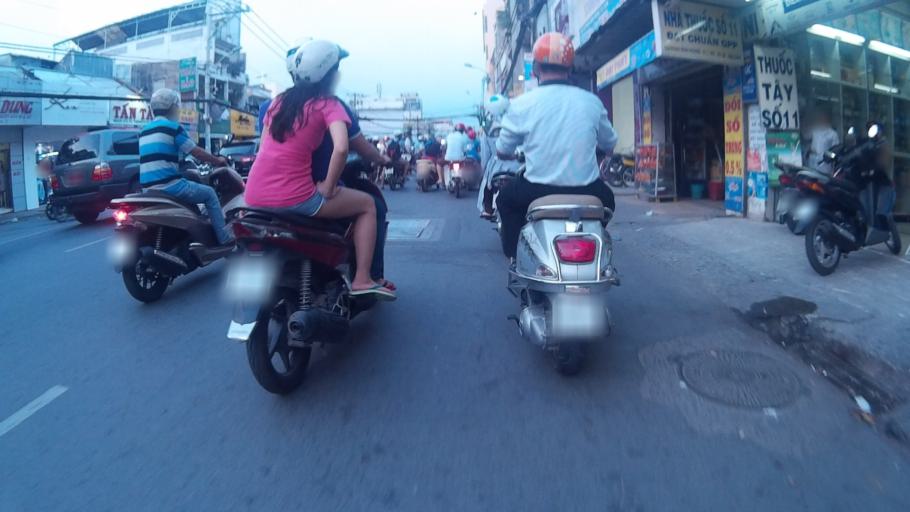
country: VN
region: Ho Chi Minh City
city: Quan Phu Nhuan
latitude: 10.7984
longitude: 106.6805
